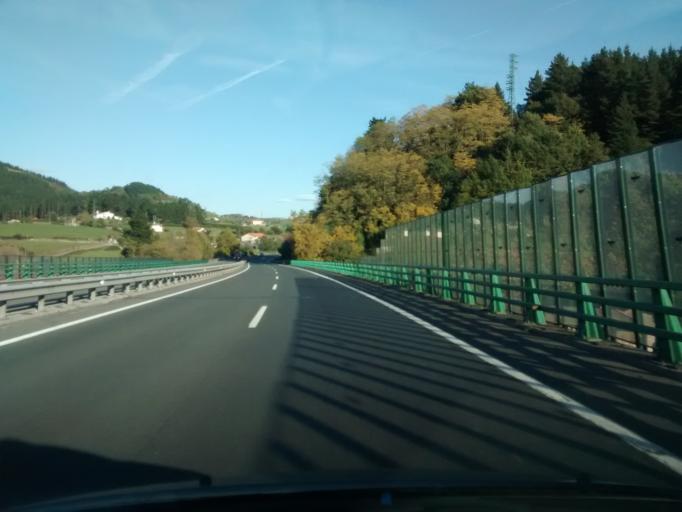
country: ES
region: Basque Country
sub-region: Bizkaia
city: Berriz
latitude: 43.1676
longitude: -2.5744
